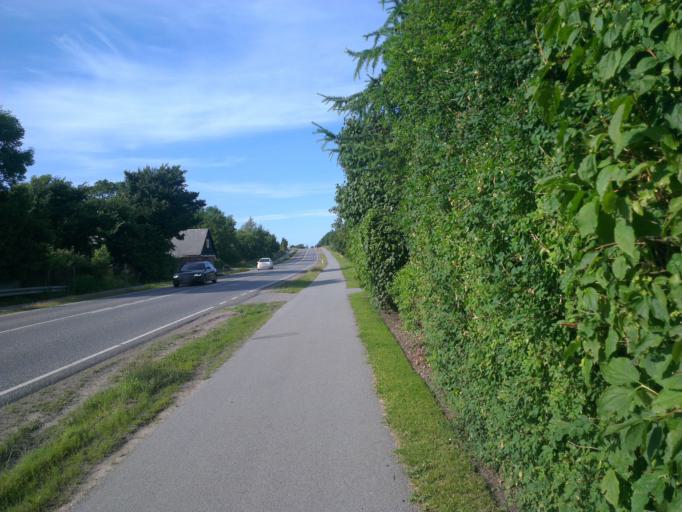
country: DK
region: Capital Region
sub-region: Frederikssund Kommune
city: Skibby
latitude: 55.7647
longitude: 11.9581
